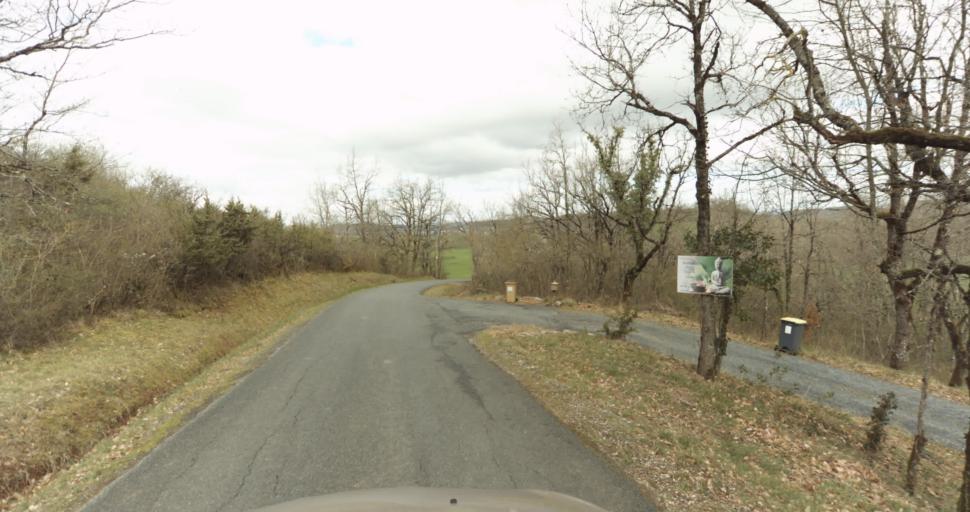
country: FR
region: Midi-Pyrenees
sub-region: Departement du Tarn
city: Frejairolles
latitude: 43.8732
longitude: 2.1950
